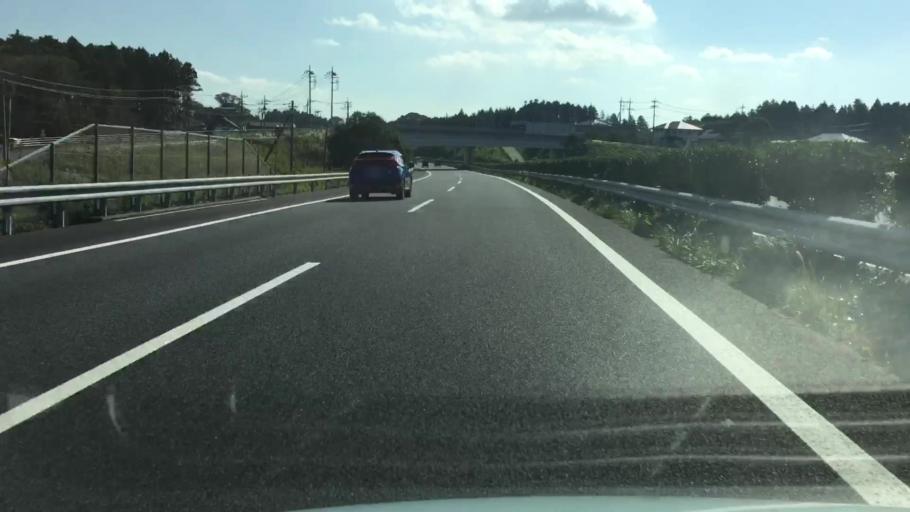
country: JP
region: Ibaraki
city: Tomobe
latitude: 36.3171
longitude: 140.3123
